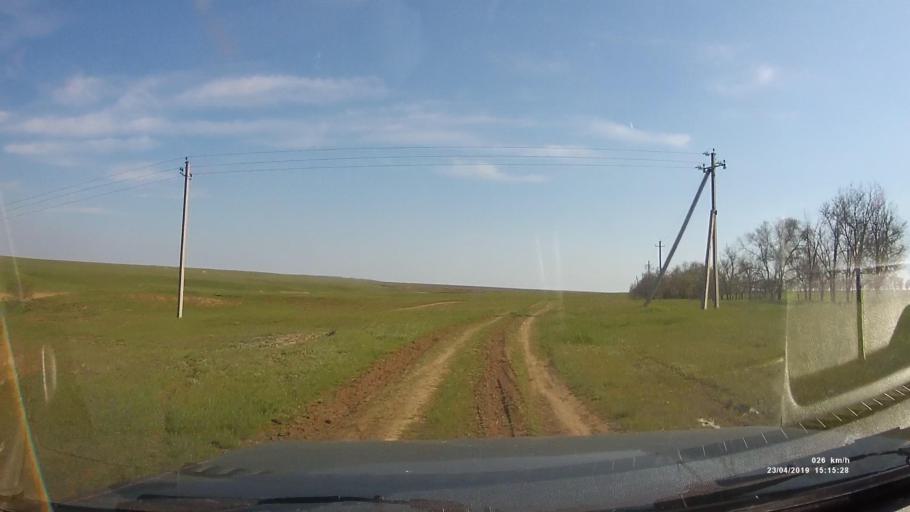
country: RU
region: Rostov
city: Remontnoye
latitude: 46.5388
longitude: 42.9695
